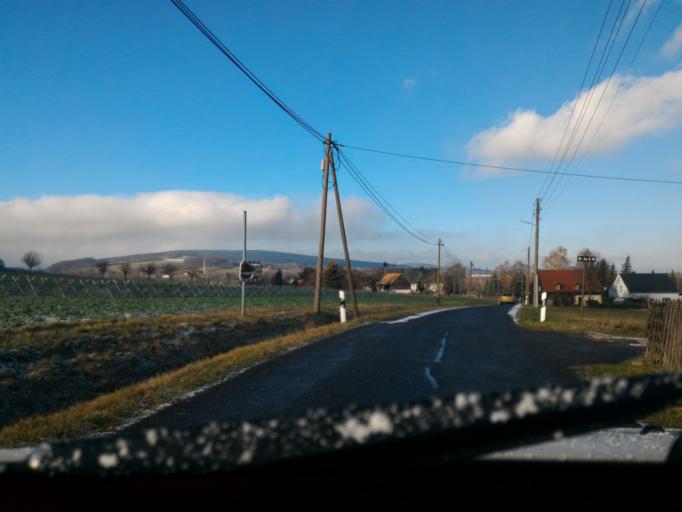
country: CZ
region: Ustecky
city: Varnsdorf
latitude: 50.8772
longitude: 14.6401
